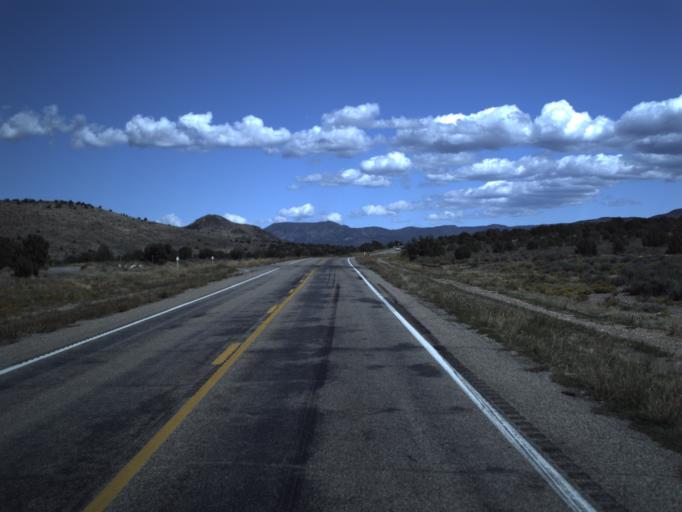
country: US
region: Utah
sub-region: Washington County
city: Ivins
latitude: 37.3551
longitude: -113.6816
